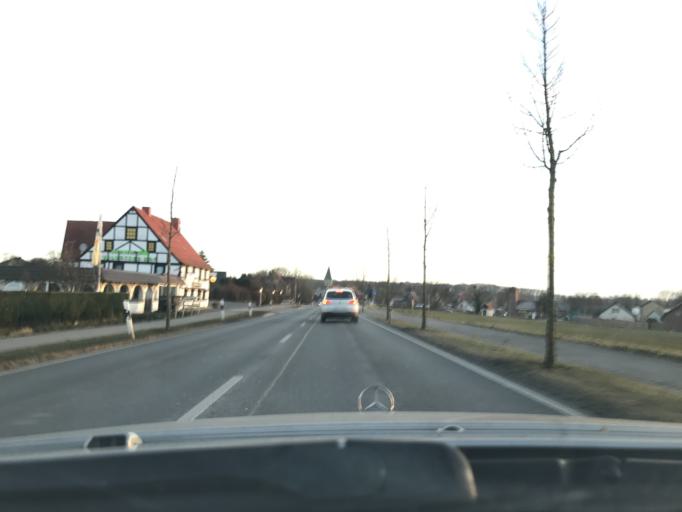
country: DE
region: North Rhine-Westphalia
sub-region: Regierungsbezirk Arnsberg
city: Werl
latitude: 51.5817
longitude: 7.8611
